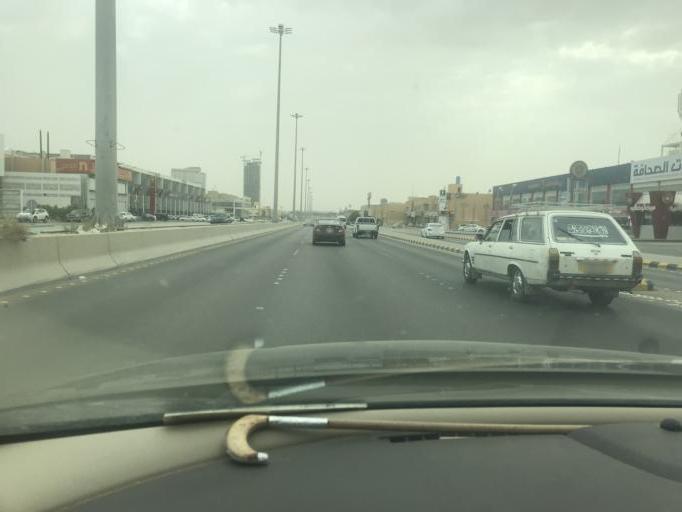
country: SA
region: Ar Riyad
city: Riyadh
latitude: 24.8165
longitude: 46.6371
